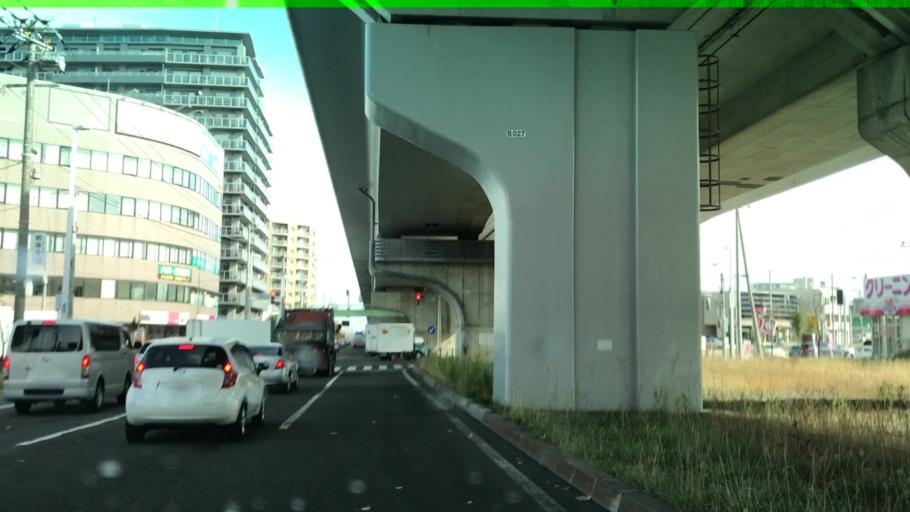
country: JP
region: Hokkaido
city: Sapporo
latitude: 43.0912
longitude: 141.2741
